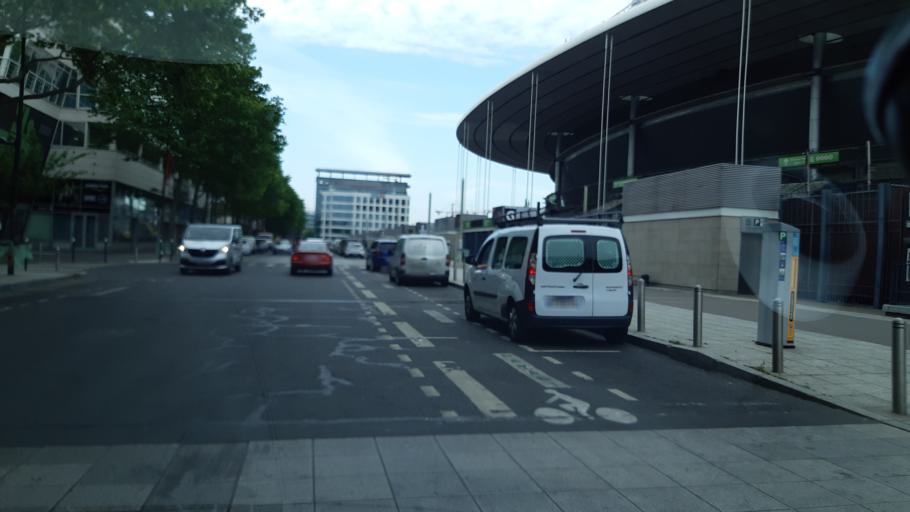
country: FR
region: Ile-de-France
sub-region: Departement de Seine-Saint-Denis
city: Saint-Denis
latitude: 48.9257
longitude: 2.3624
